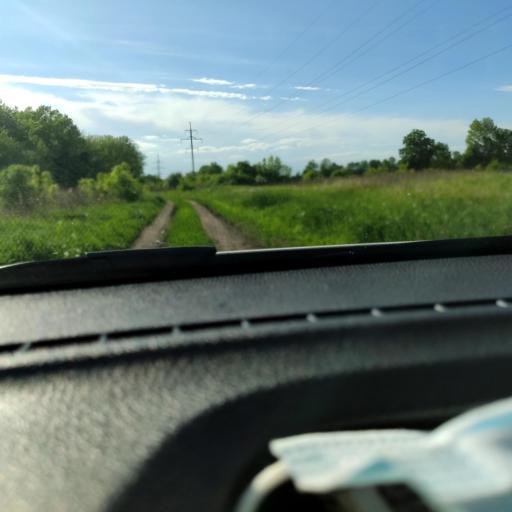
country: RU
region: Voronezj
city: Ramon'
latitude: 51.9468
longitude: 39.3652
